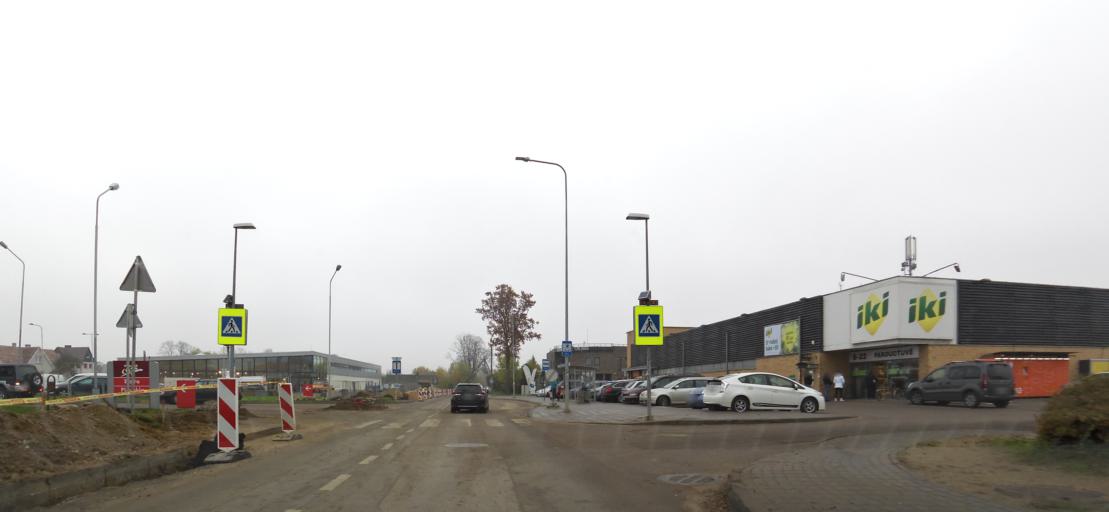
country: LT
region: Vilnius County
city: Rasos
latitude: 54.6626
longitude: 25.3417
